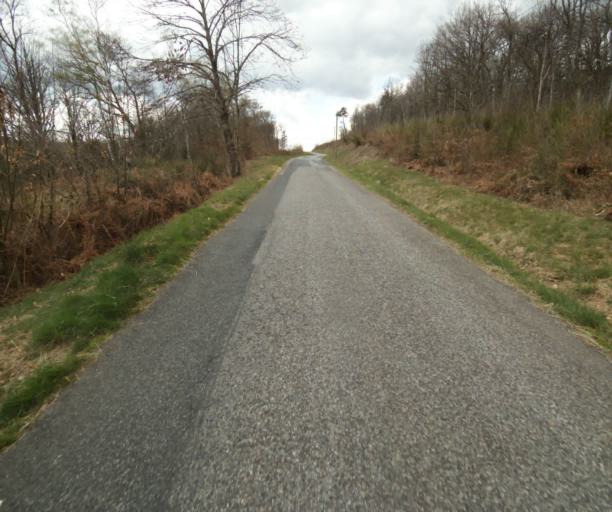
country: FR
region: Limousin
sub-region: Departement de la Correze
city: Correze
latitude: 45.2652
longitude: 1.9020
